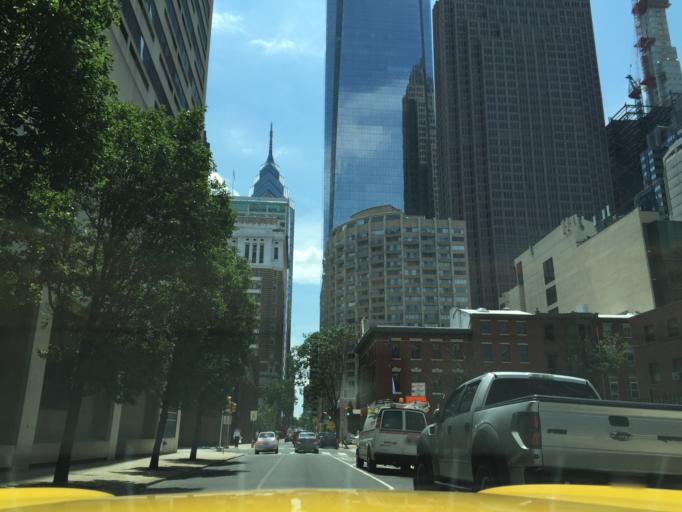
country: US
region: Pennsylvania
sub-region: Philadelphia County
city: Philadelphia
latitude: 39.9573
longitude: -75.1675
